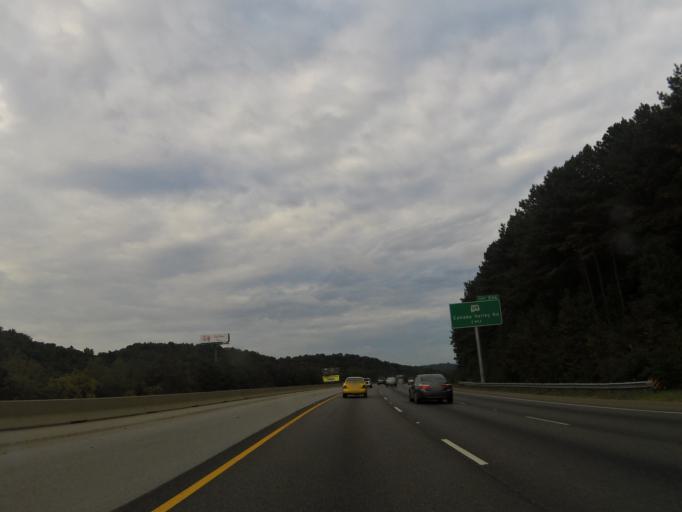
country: US
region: Alabama
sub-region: Shelby County
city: Pelham
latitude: 33.3203
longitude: -86.7867
